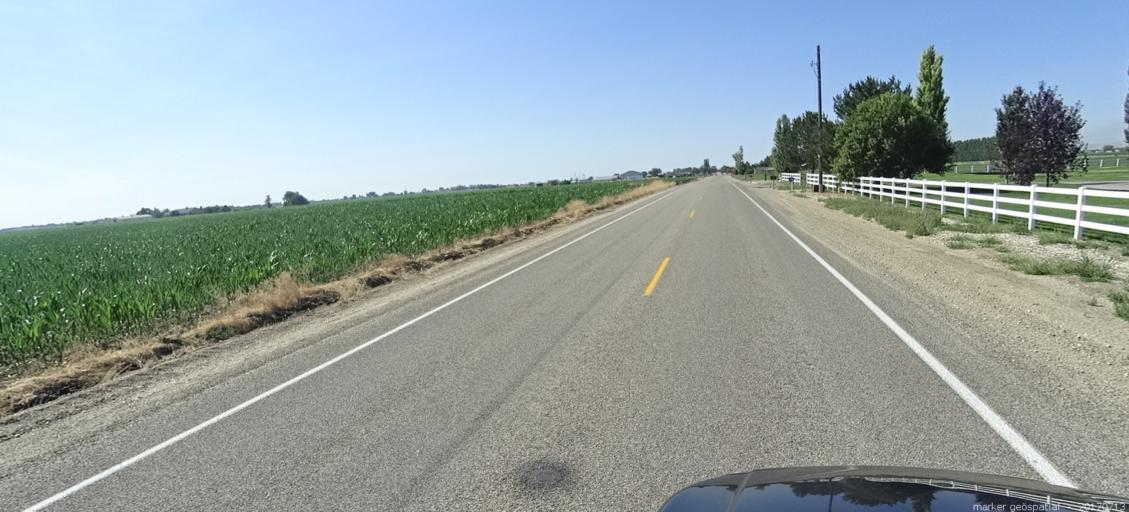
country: US
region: Idaho
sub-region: Ada County
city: Kuna
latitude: 43.5209
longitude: -116.3743
